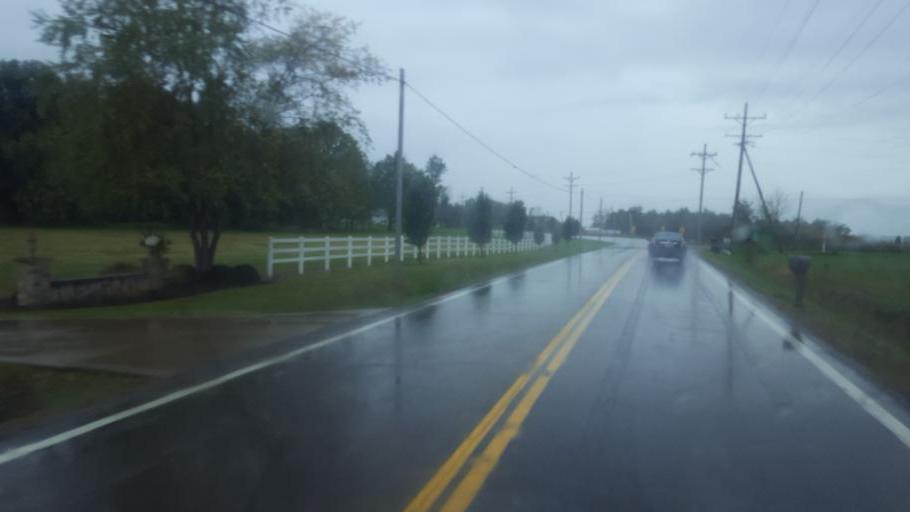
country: US
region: Ohio
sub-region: Richland County
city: Lincoln Heights
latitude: 40.8184
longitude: -82.4872
